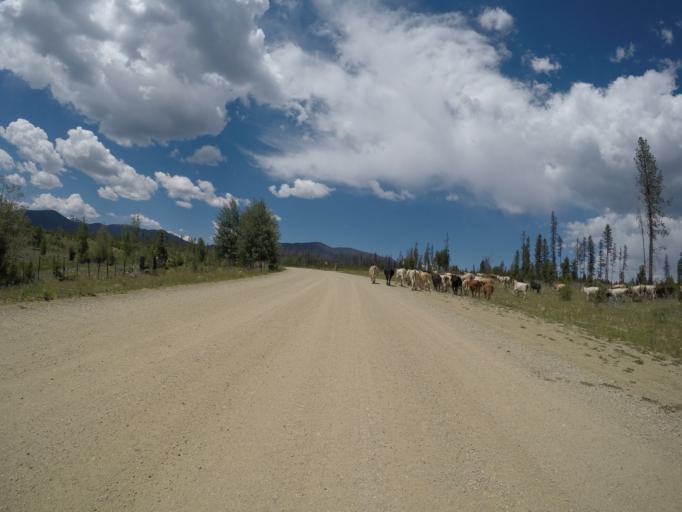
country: US
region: Colorado
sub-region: Grand County
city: Fraser
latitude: 39.9625
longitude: -105.8677
